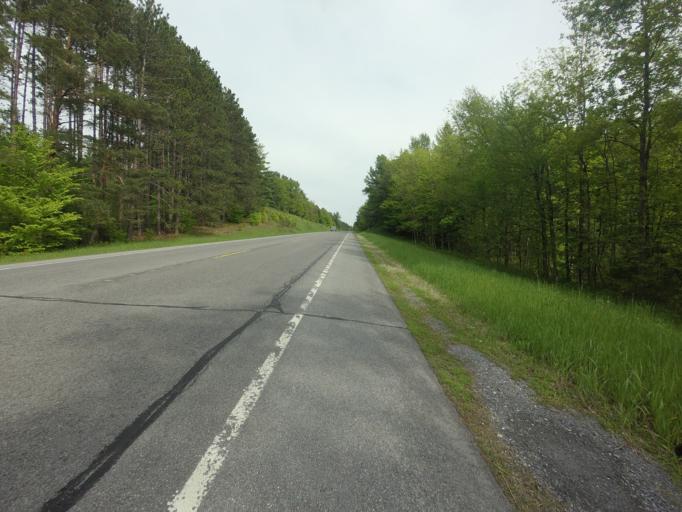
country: US
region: New York
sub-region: St. Lawrence County
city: Gouverneur
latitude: 44.2885
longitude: -75.2134
